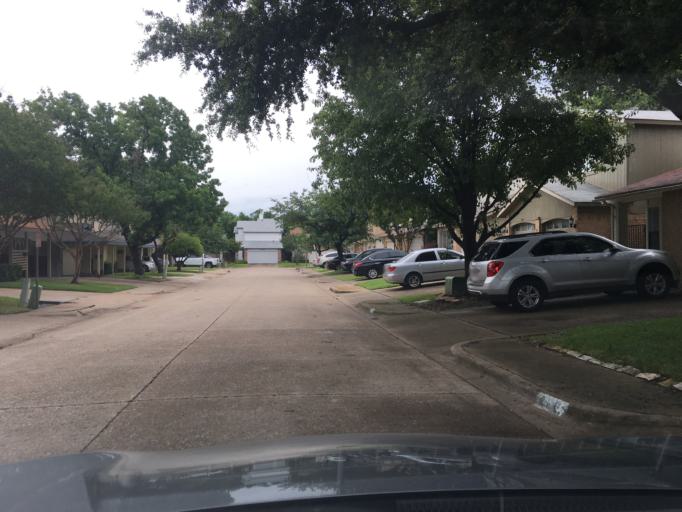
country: US
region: Texas
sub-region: Dallas County
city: Garland
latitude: 32.9506
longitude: -96.6707
